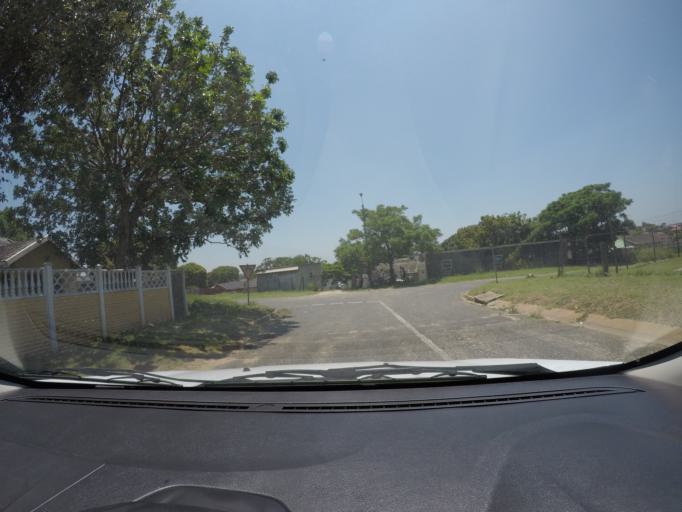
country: ZA
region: KwaZulu-Natal
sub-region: uThungulu District Municipality
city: eSikhawini
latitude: -28.8779
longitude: 31.9063
